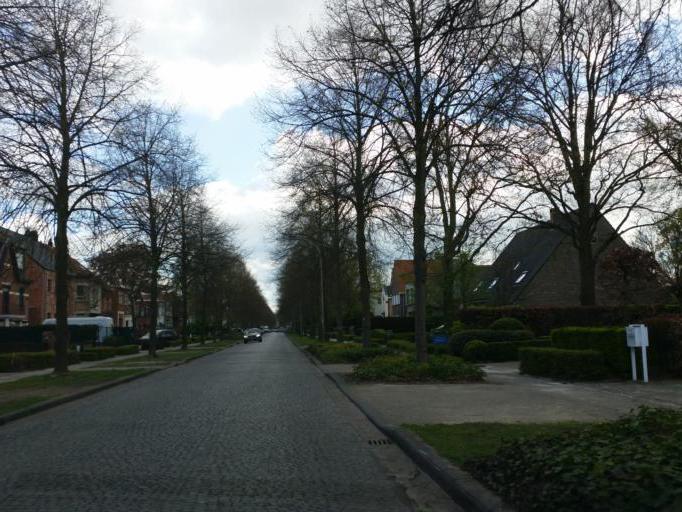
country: BE
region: Flanders
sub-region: Provincie Antwerpen
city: Brasschaat
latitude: 51.2941
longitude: 4.4844
